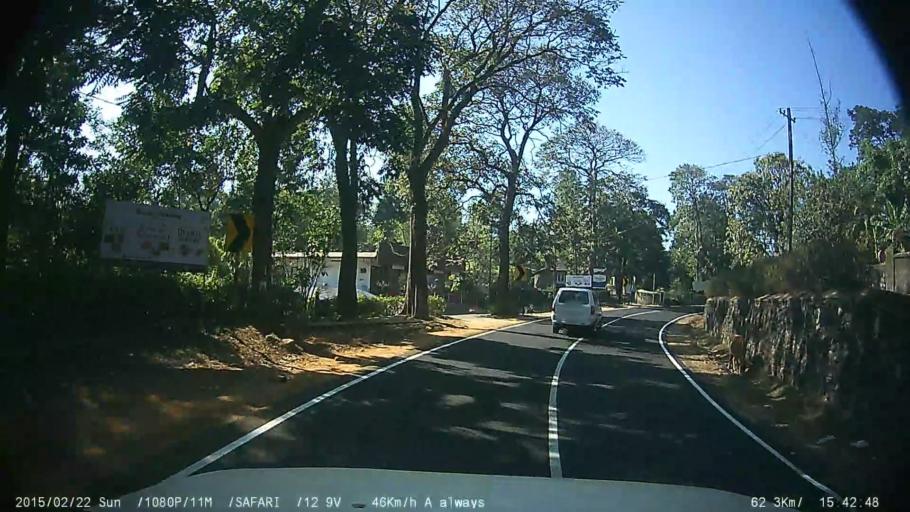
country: IN
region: Kerala
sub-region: Kottayam
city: Erattupetta
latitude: 9.5792
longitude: 76.9704
